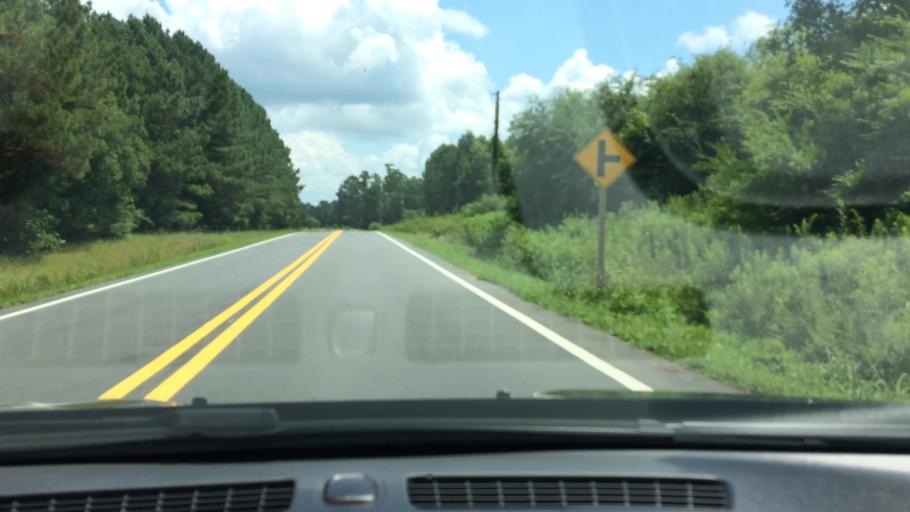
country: US
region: North Carolina
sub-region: Craven County
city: Vanceboro
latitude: 35.4300
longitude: -77.1791
